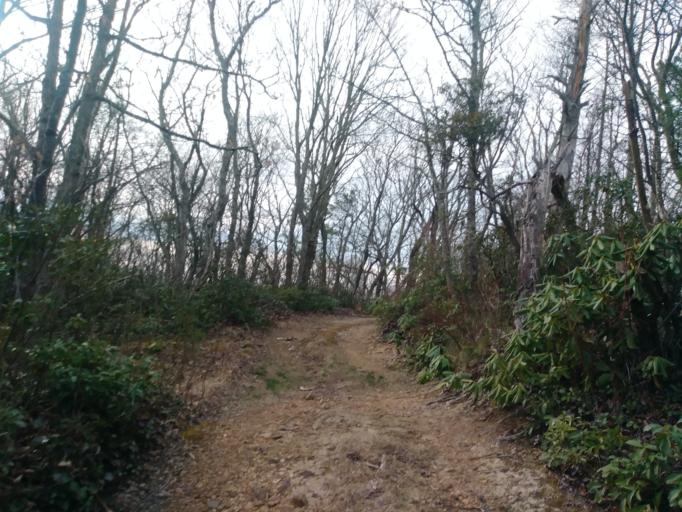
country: US
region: Tennessee
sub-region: Greene County
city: Tusculum
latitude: 36.0568
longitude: -82.6737
